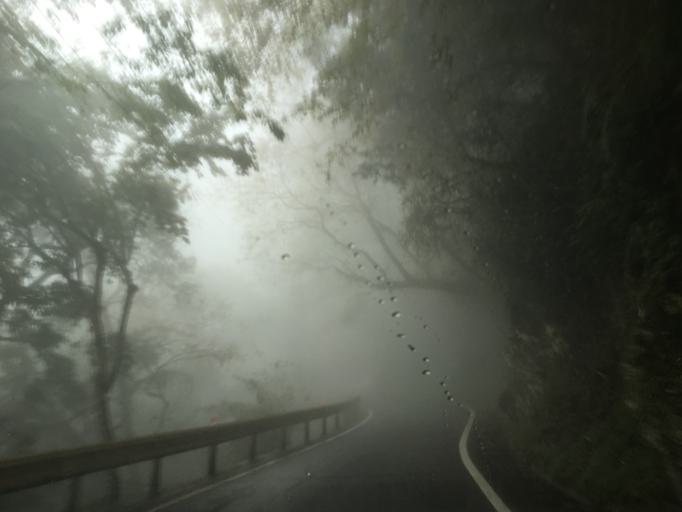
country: TW
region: Taiwan
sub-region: Hualien
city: Hualian
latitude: 24.1886
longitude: 121.4210
